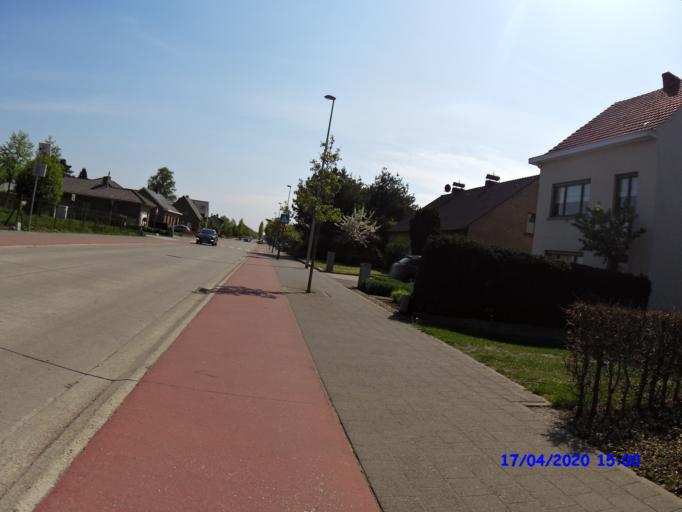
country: BE
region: Flanders
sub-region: Provincie Antwerpen
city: Oud-Turnhout
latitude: 51.3342
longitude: 4.9733
